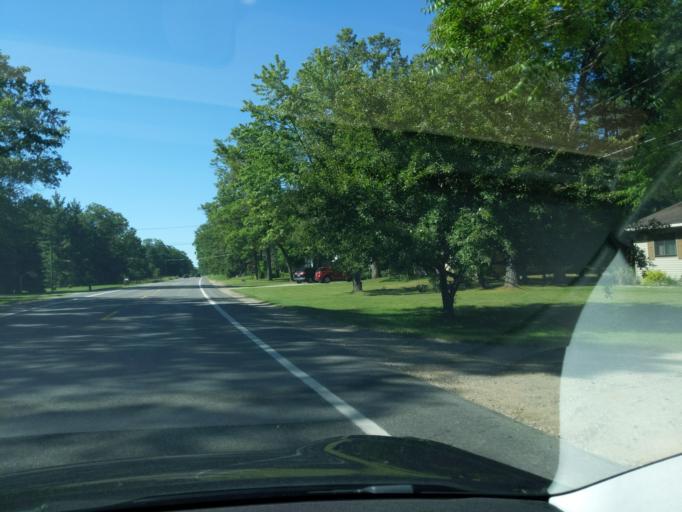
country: US
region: Michigan
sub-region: Muskegon County
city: Lakewood Club
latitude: 43.3688
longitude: -86.2818
